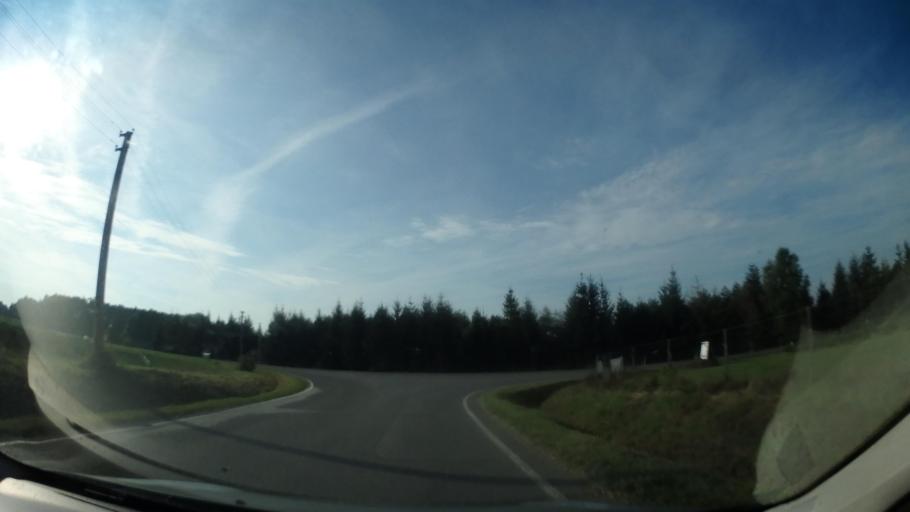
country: CZ
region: Jihocesky
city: Cimelice
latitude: 49.4368
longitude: 14.1444
